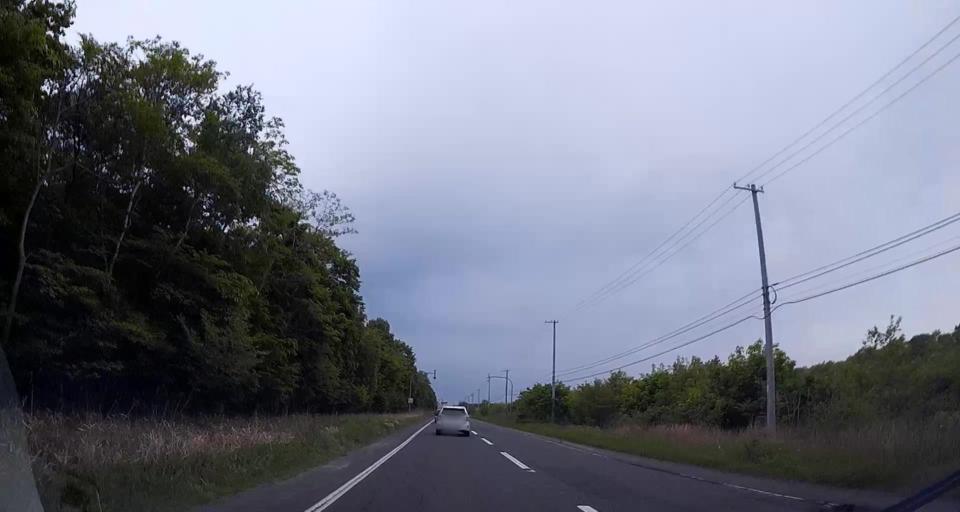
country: JP
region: Hokkaido
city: Tomakomai
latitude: 42.6900
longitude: 141.7289
